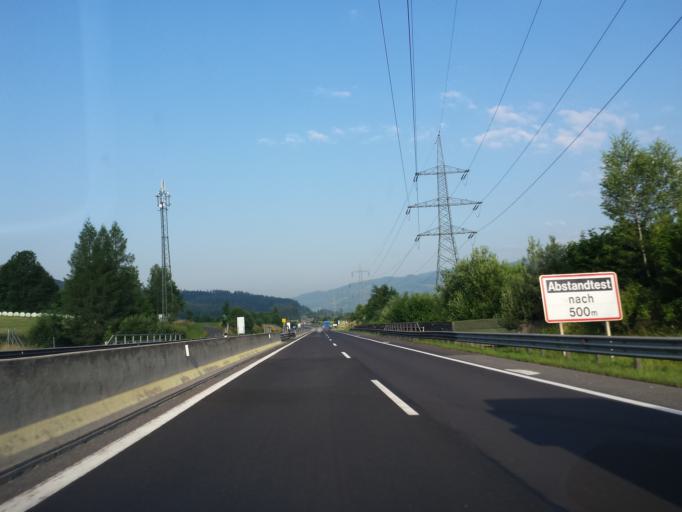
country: AT
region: Styria
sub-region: Politischer Bezirk Bruck-Muerzzuschlag
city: Krieglach
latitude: 47.5371
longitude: 15.5603
